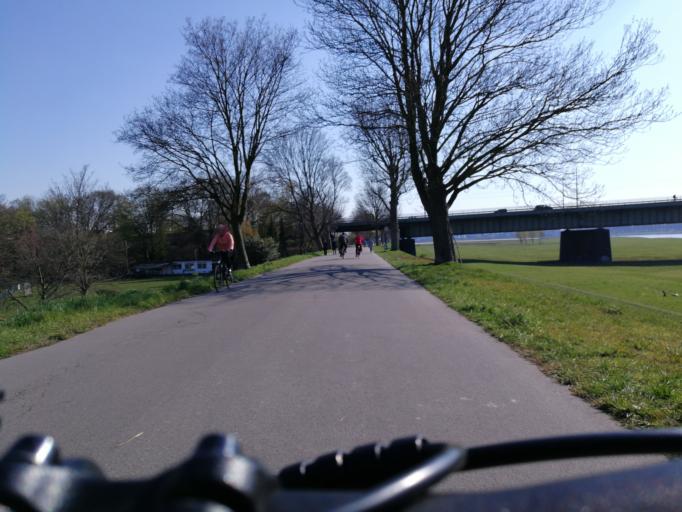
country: DE
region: North Rhine-Westphalia
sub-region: Regierungsbezirk Dusseldorf
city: Dusseldorf
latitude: 51.1999
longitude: 6.7359
